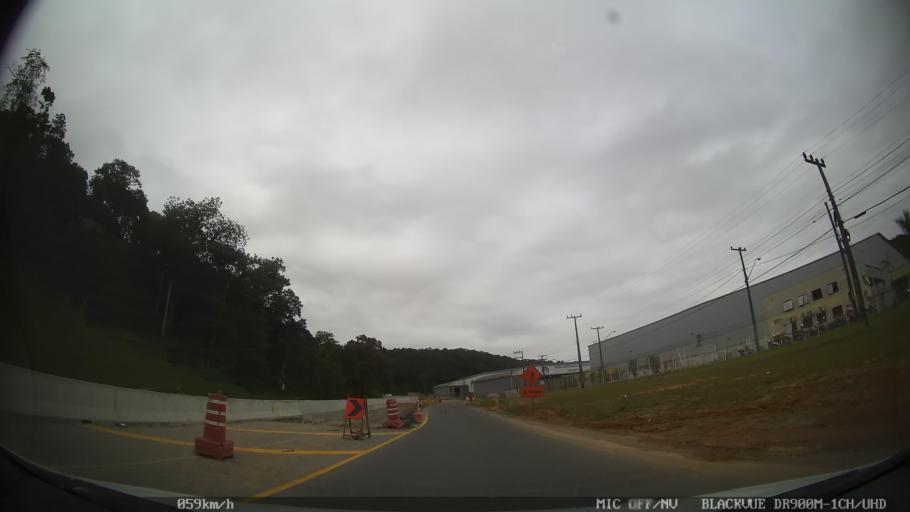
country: BR
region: Santa Catarina
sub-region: Joinville
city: Joinville
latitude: -26.2572
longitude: -48.9015
